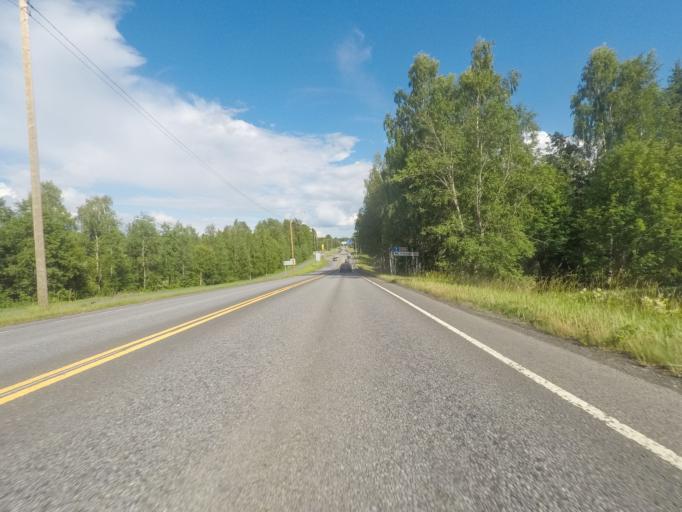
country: FI
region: Southern Savonia
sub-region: Mikkeli
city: Mikkeli
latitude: 61.7040
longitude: 27.3489
